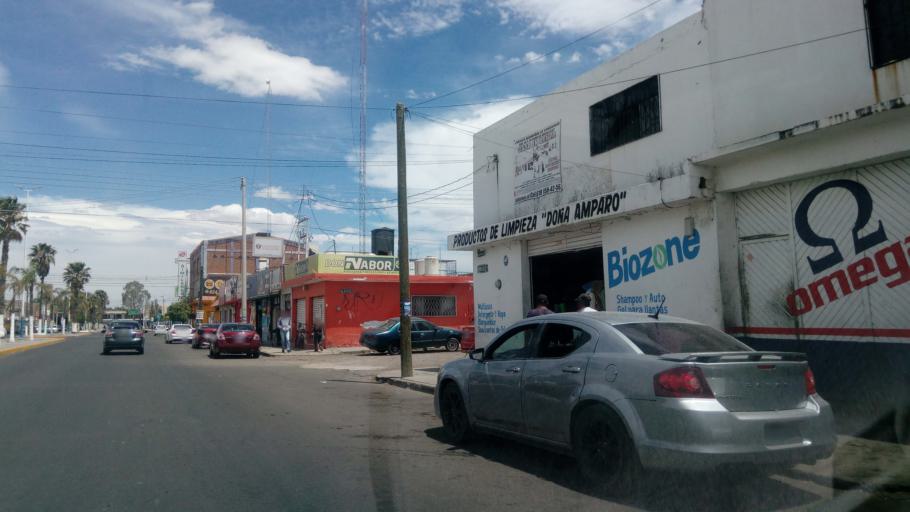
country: MX
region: Durango
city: Victoria de Durango
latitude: 23.9960
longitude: -104.6658
